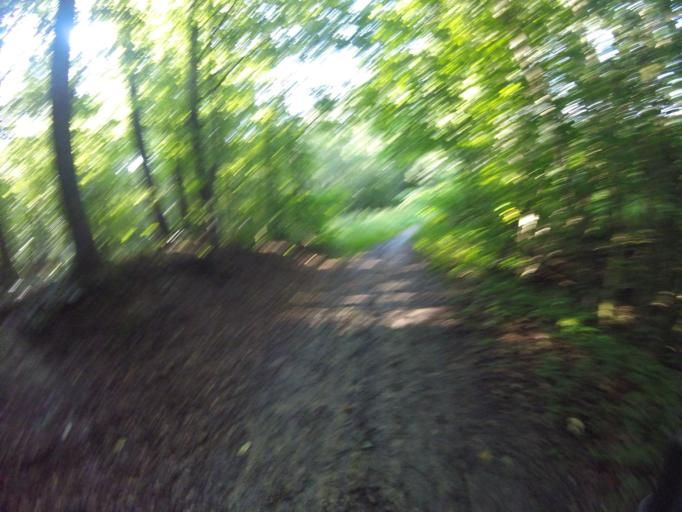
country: HU
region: Zala
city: Becsehely
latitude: 46.4997
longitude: 16.7378
